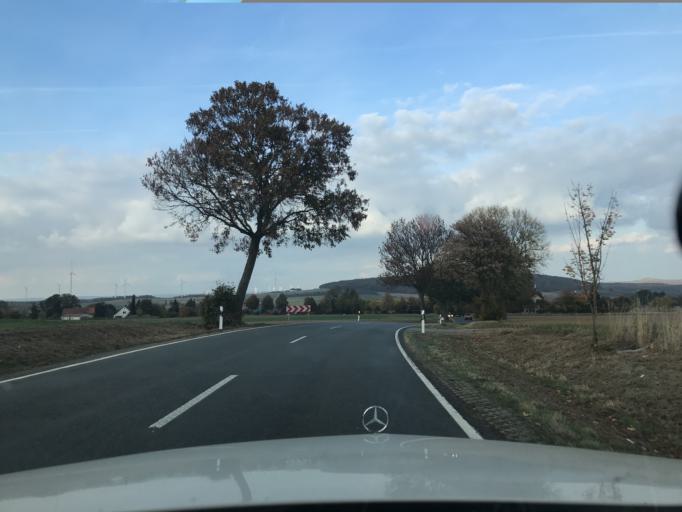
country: DE
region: Hesse
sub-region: Regierungsbezirk Kassel
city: Breuna
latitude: 51.4379
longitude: 9.2342
